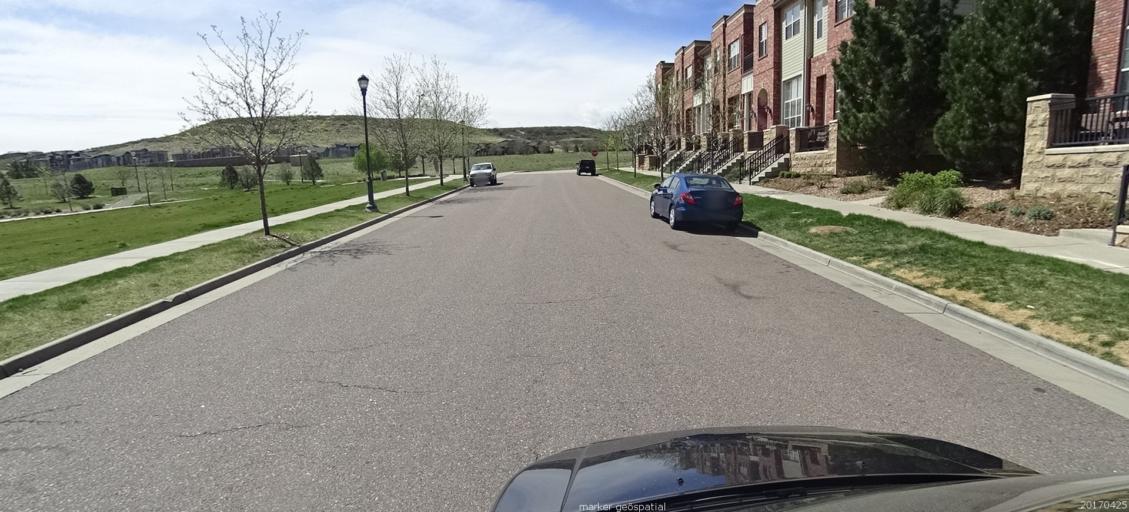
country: US
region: Colorado
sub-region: Douglas County
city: Carriage Club
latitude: 39.5293
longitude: -104.8813
